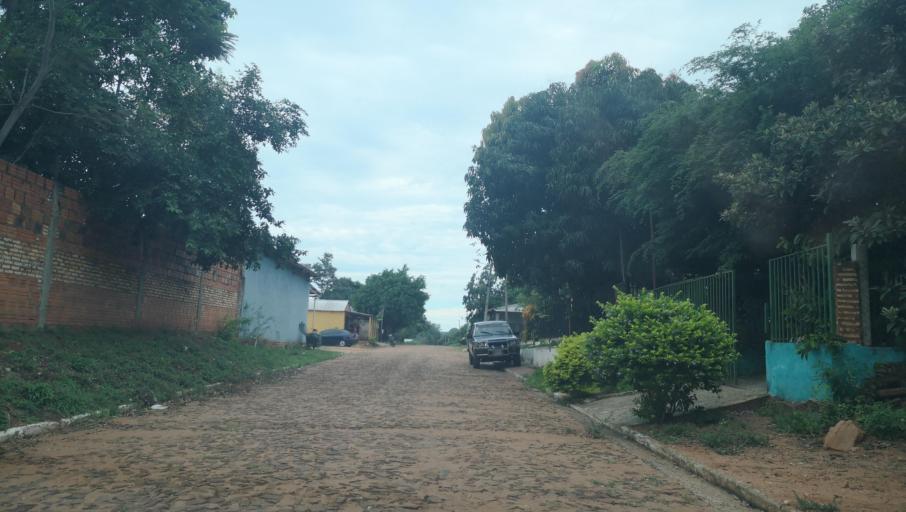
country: PY
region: San Pedro
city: Capiibary
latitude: -24.7328
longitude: -56.0224
